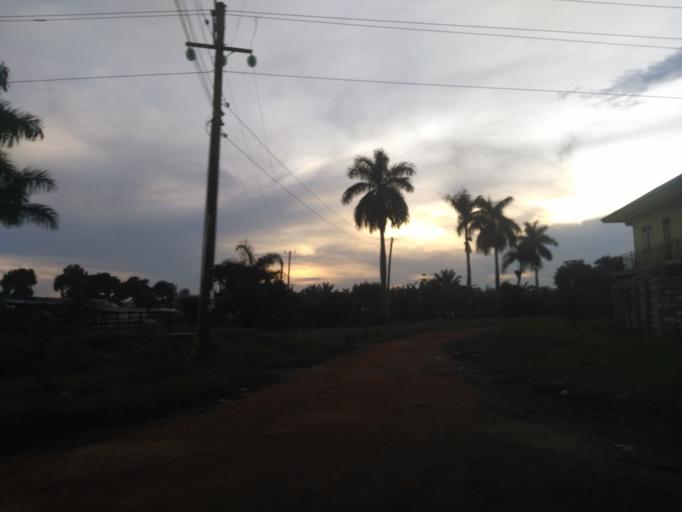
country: UG
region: Eastern Region
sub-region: Jinja District
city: Jinja
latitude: 0.4292
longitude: 33.1988
